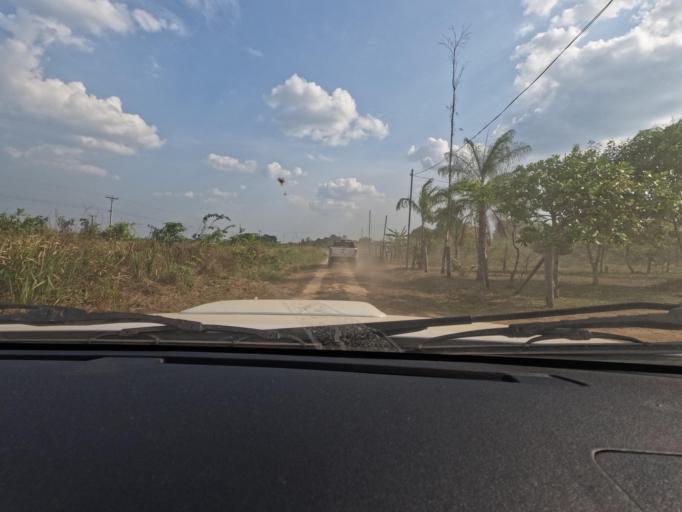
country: BR
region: Rondonia
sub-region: Porto Velho
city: Porto Velho
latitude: -8.5738
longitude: -63.9924
